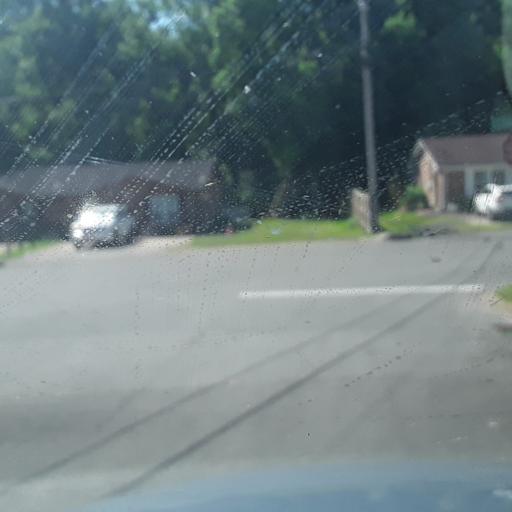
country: US
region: Tennessee
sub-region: Williamson County
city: Brentwood Estates
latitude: 36.0360
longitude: -86.7050
